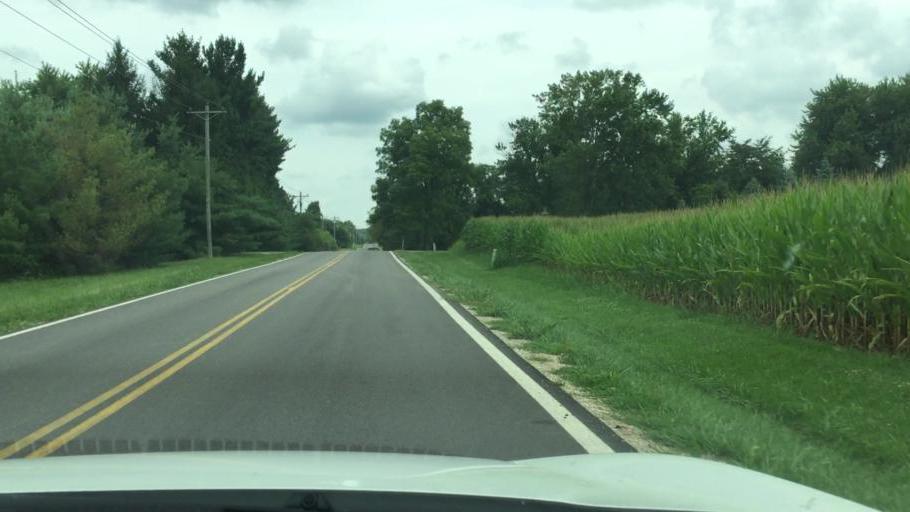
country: US
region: Ohio
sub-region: Union County
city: Marysville
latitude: 40.2166
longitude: -83.4538
